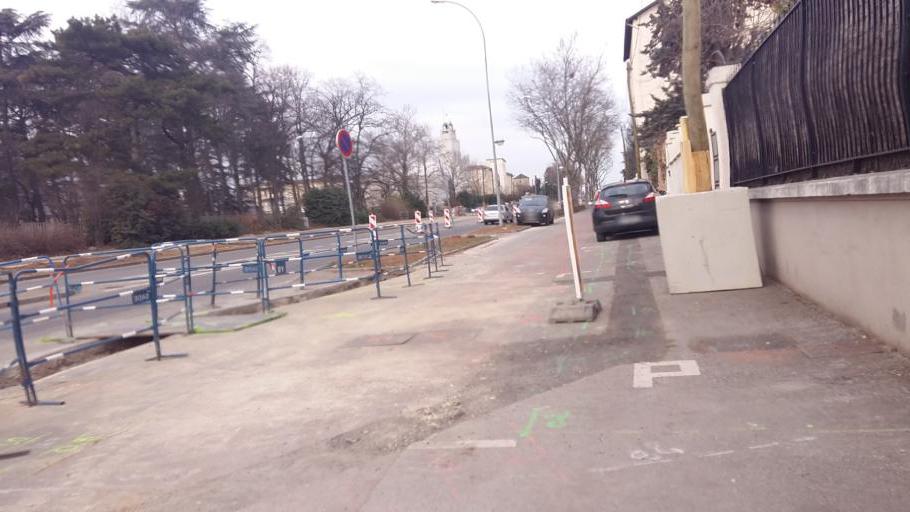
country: FR
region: Rhone-Alpes
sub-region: Departement du Rhone
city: Bron
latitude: 45.7352
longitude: 4.8900
